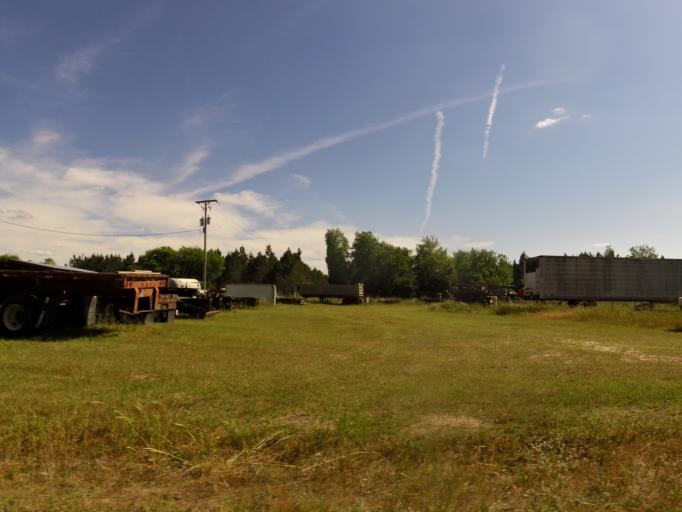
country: US
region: South Carolina
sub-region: Barnwell County
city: Blackville
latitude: 33.3484
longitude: -81.2146
